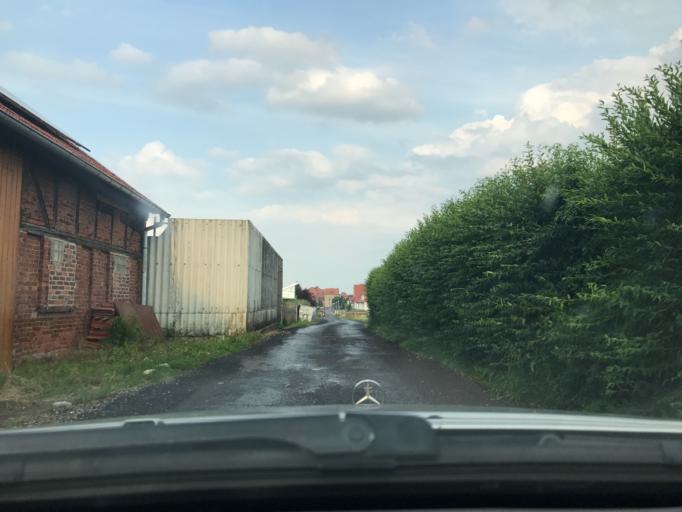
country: DE
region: Thuringia
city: Dingelstadt
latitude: 51.3126
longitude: 10.3132
